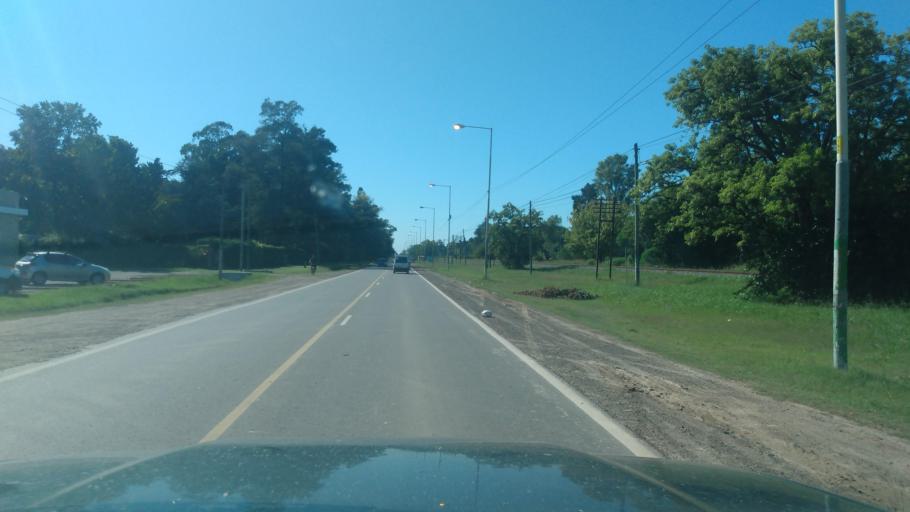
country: AR
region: Buenos Aires
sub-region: Partido de General Rodriguez
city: General Rodriguez
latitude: -34.6022
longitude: -58.9805
